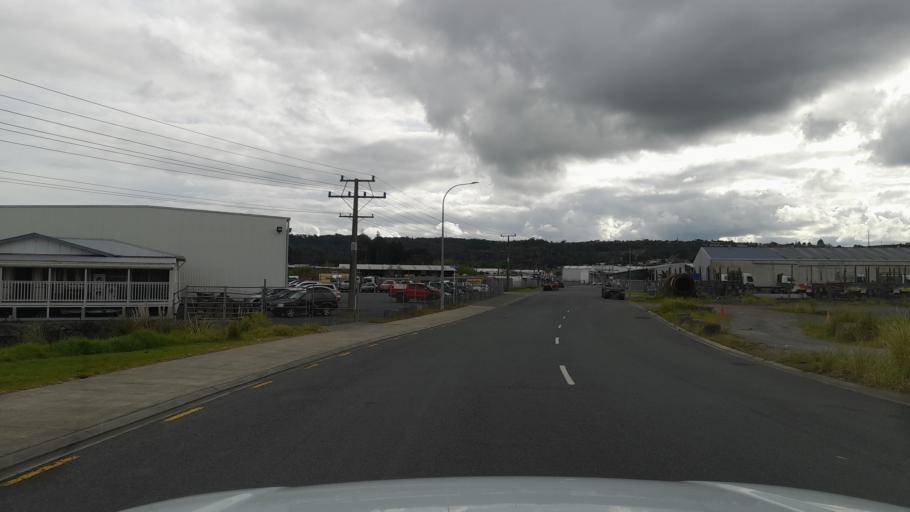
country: NZ
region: Northland
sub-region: Whangarei
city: Whangarei
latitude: -35.7484
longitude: 174.3163
